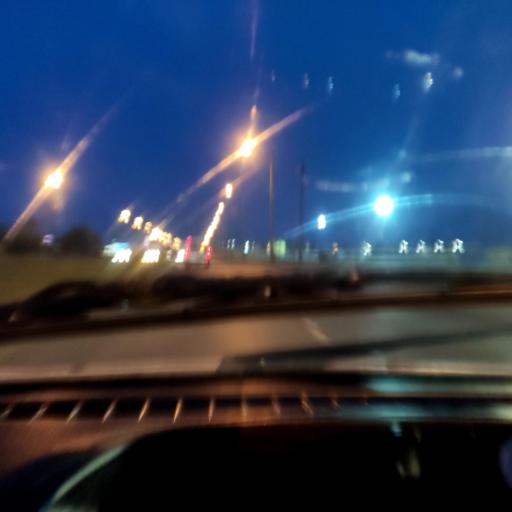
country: RU
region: Samara
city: Tol'yatti
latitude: 53.5563
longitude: 49.3453
